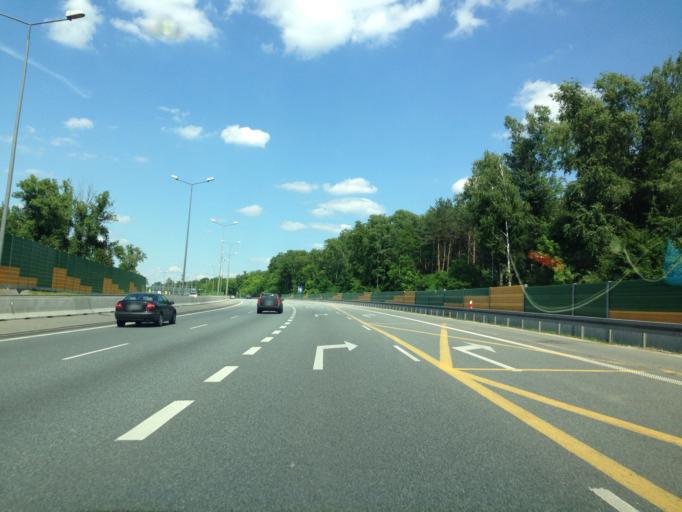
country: PL
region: Masovian Voivodeship
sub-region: Warszawa
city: Bemowo
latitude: 52.2515
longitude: 20.9424
